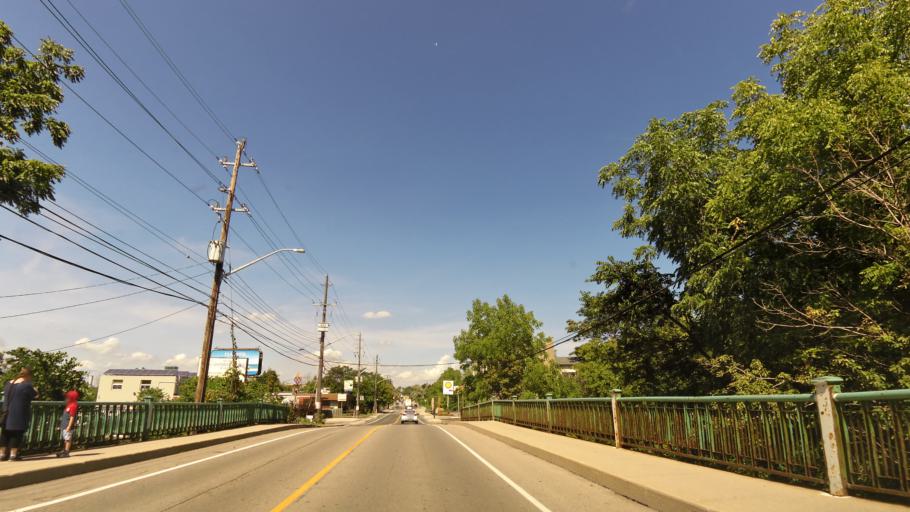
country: CA
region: Ontario
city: Hamilton
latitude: 43.2564
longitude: -79.8901
